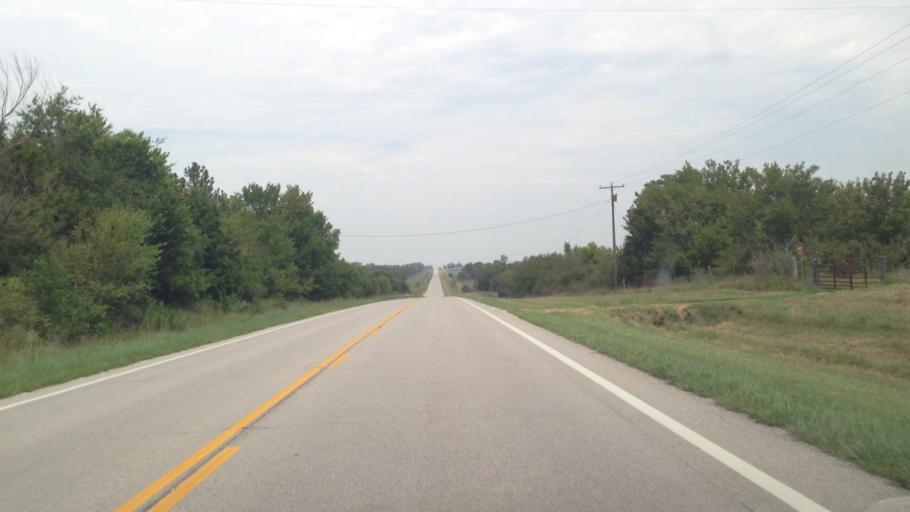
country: US
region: Kansas
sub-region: Neosho County
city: Erie
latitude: 37.6557
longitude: -95.2517
